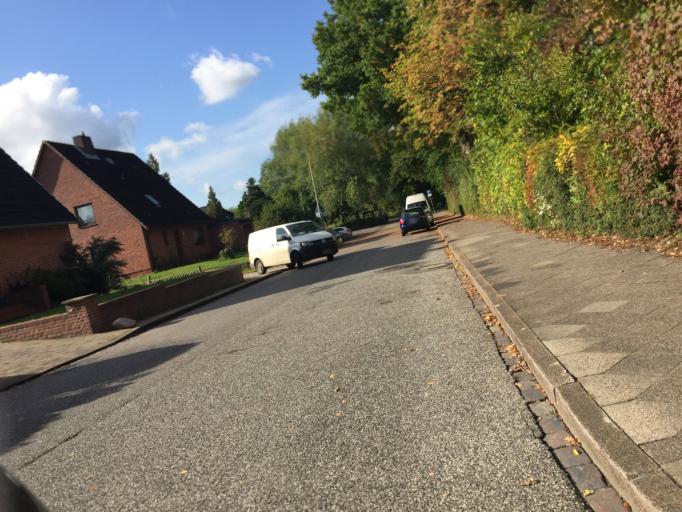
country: DE
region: Schleswig-Holstein
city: Heiligenstedten
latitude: 53.9364
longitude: 9.4917
